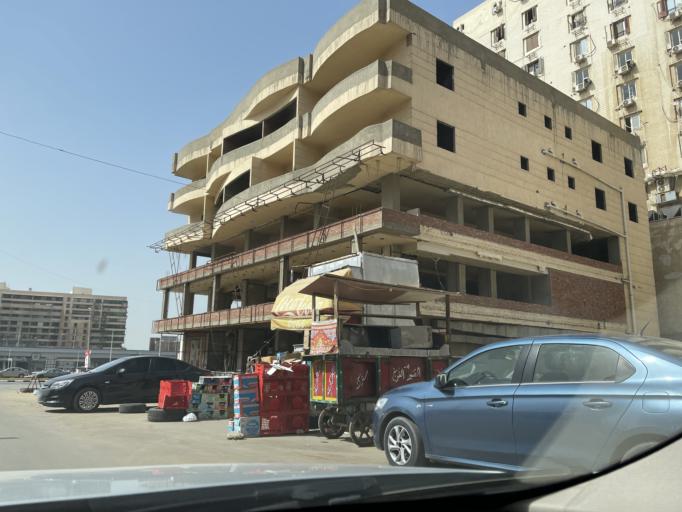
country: EG
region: Muhafazat al Qahirah
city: Cairo
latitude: 30.0691
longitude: 31.3549
